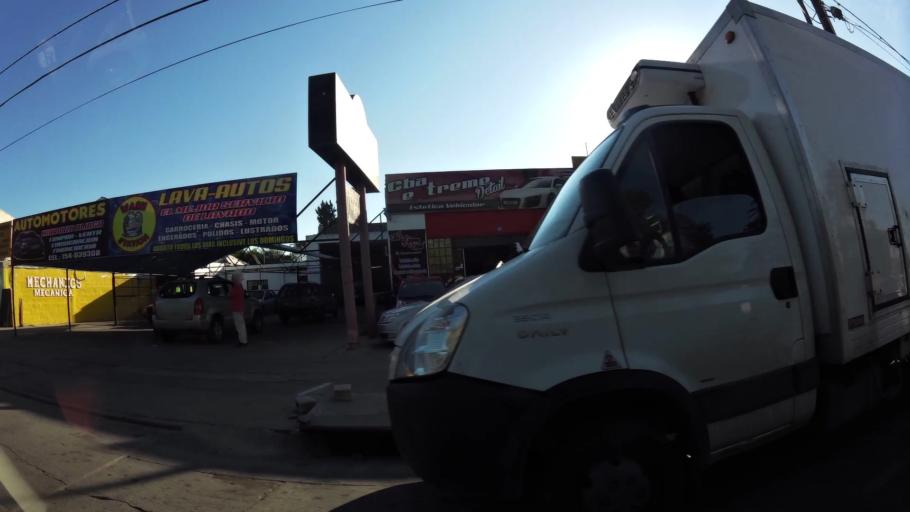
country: AR
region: Cordoba
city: Villa Allende
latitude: -31.3546
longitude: -64.2440
